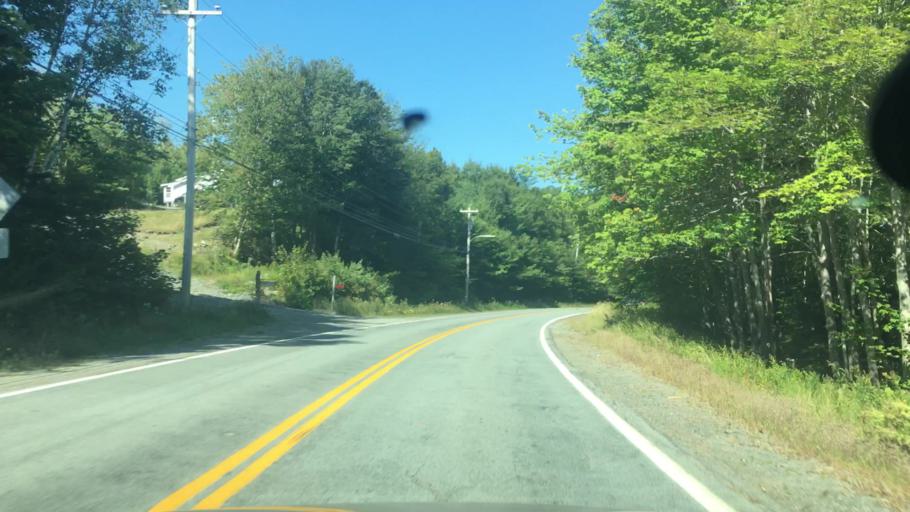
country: CA
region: Nova Scotia
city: New Glasgow
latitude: 44.9180
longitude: -62.5412
